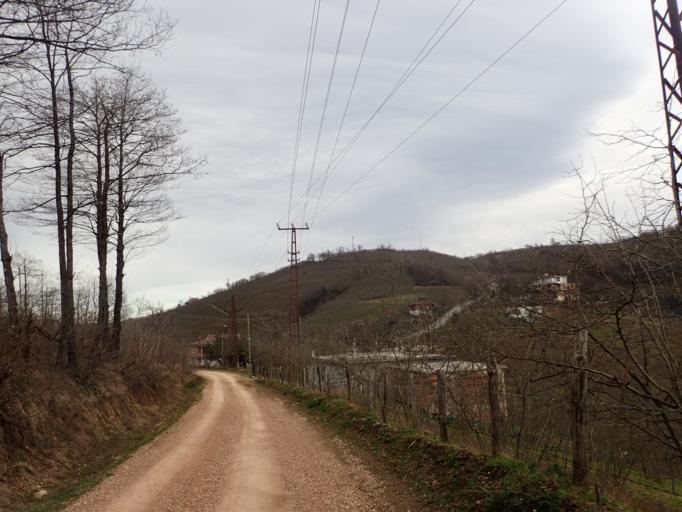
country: TR
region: Ordu
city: Camas
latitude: 40.8894
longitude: 37.5236
